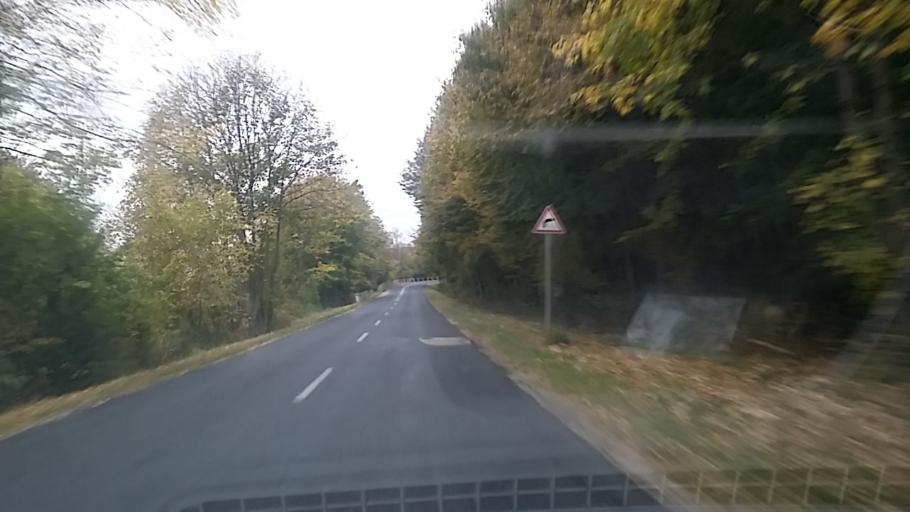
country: HU
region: Veszprem
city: Zirc
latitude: 47.2458
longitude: 17.7734
